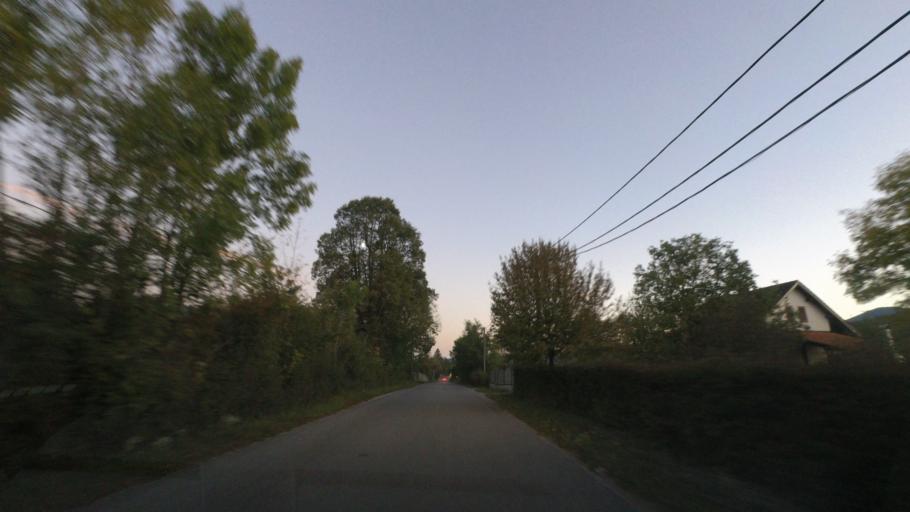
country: HR
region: Zadarska
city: Obrovac
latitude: 44.3646
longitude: 15.6513
